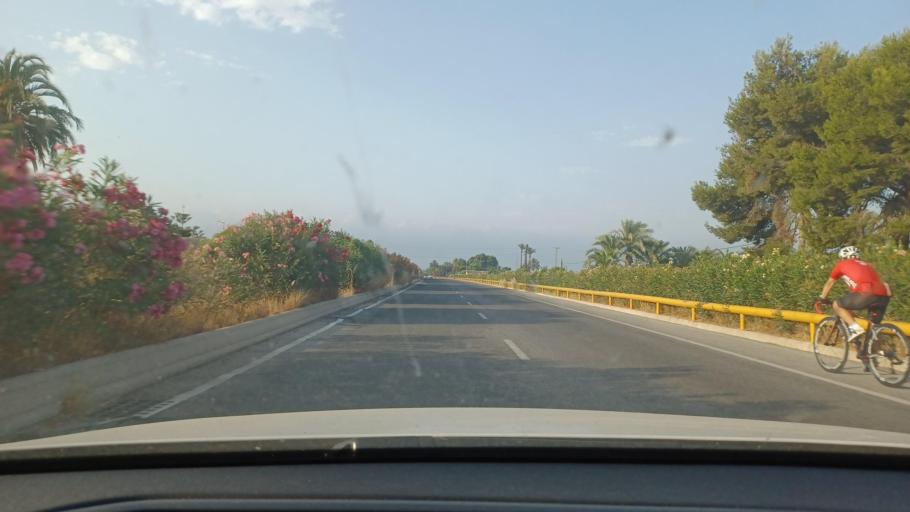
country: ES
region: Valencia
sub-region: Provincia de Alicante
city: Elche
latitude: 38.2028
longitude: -0.7002
